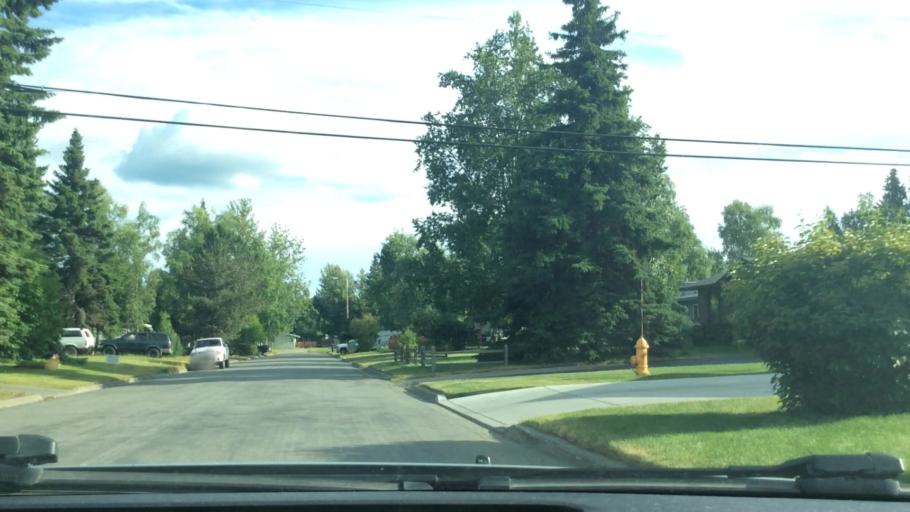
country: US
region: Alaska
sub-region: Anchorage Municipality
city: Elmendorf Air Force Base
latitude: 61.2078
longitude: -149.7560
